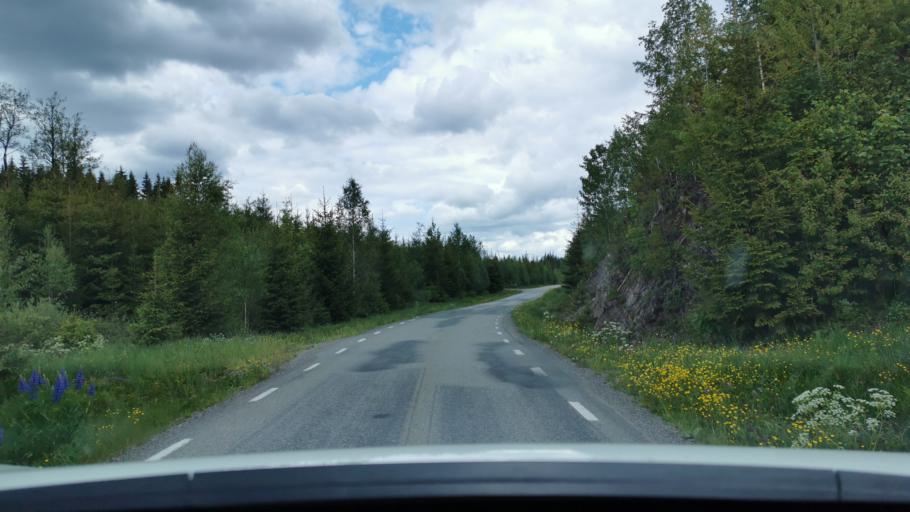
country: SE
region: Vaestra Goetaland
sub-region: Bengtsfors Kommun
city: Dals Langed
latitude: 58.8071
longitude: 12.3254
